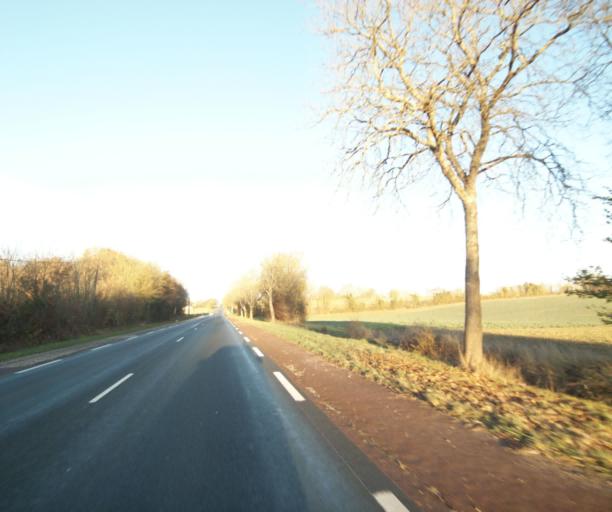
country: FR
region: Poitou-Charentes
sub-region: Departement de la Charente-Maritime
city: Saint-Georges-des-Coteaux
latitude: 45.7811
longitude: -0.7071
